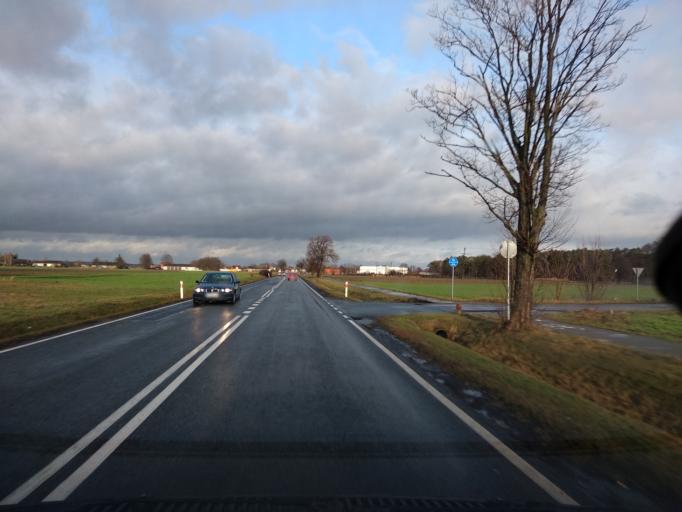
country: PL
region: Greater Poland Voivodeship
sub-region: Powiat koninski
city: Rychwal
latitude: 52.0886
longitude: 18.1639
